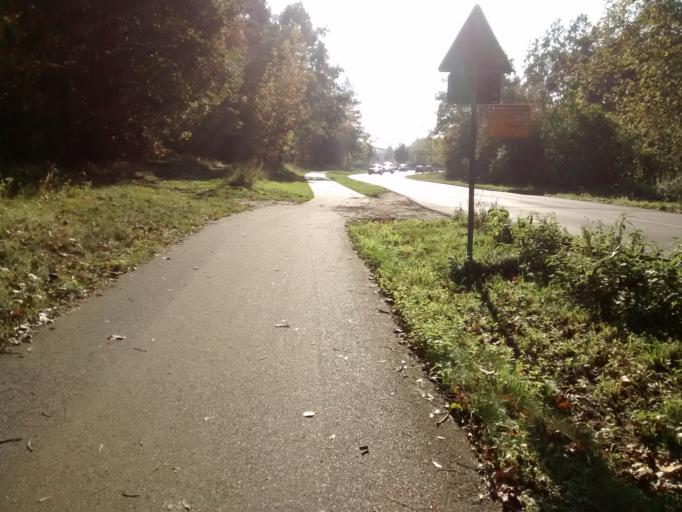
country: DE
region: Brandenburg
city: Hennigsdorf
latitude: 52.6375
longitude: 13.2208
